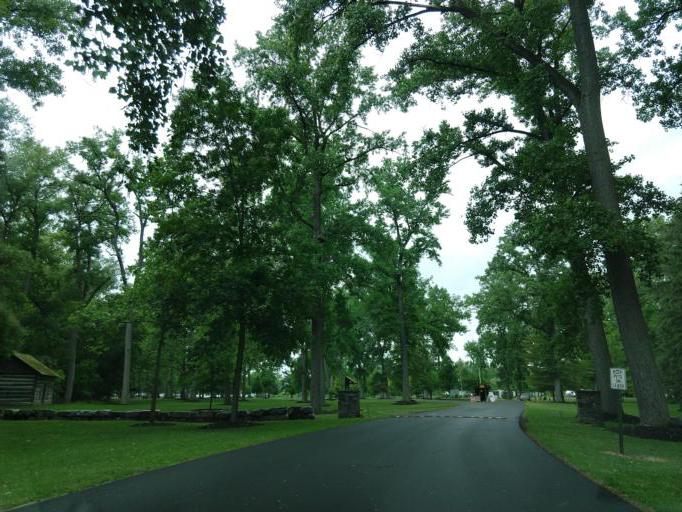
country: US
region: New York
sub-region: Tompkins County
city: Northwest Ithaca
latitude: 42.5371
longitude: -76.5441
